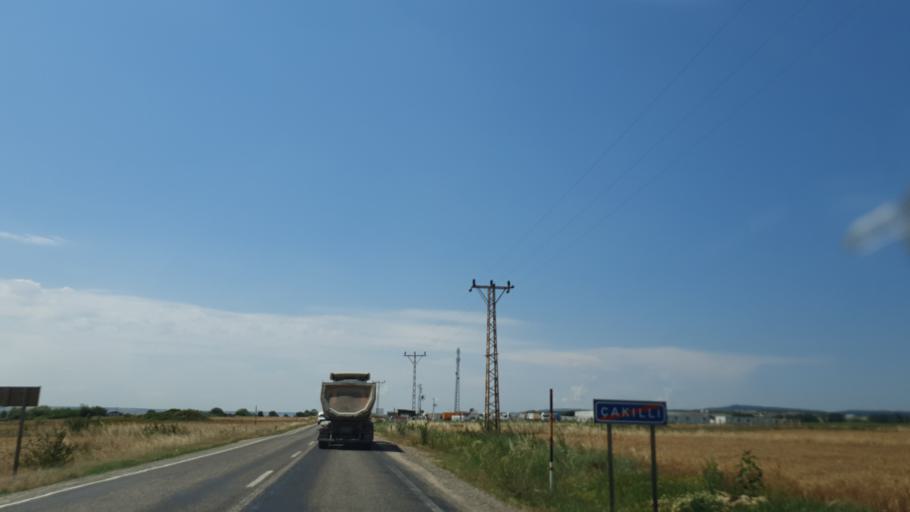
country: TR
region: Tekirdag
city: Saray
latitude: 41.5175
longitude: 27.8626
